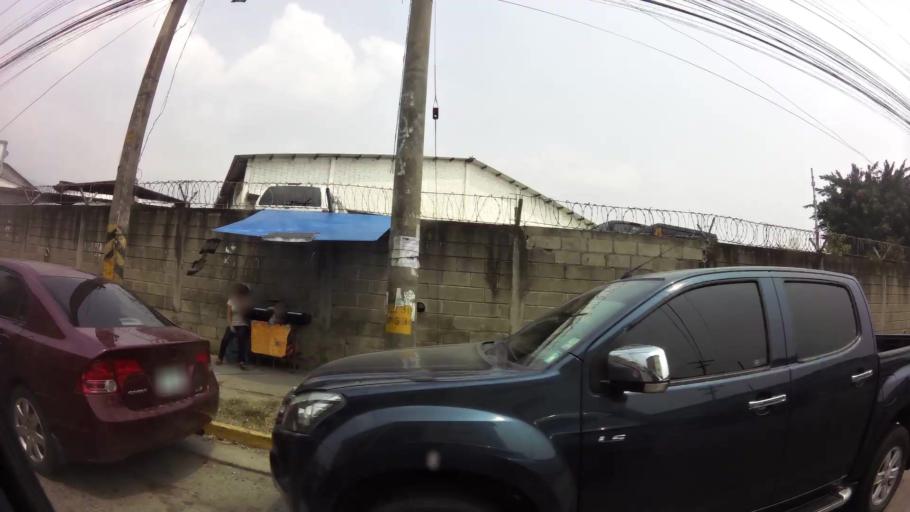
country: HN
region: Cortes
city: San Pedro Sula
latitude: 15.4855
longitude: -88.0295
